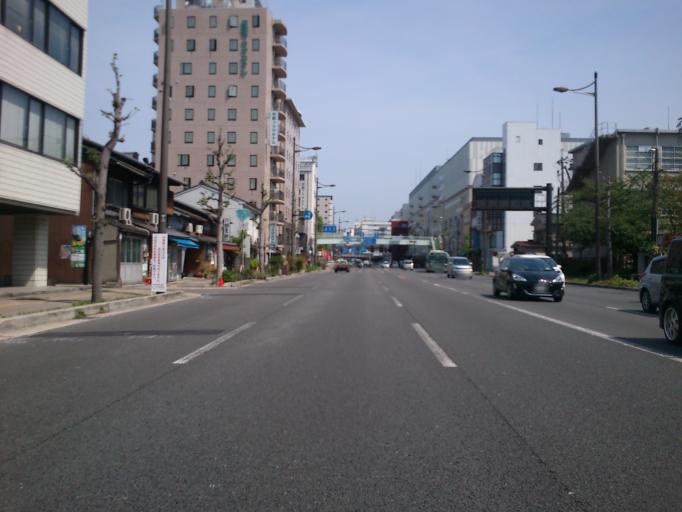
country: JP
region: Kyoto
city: Kyoto
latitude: 34.9805
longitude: 135.7537
